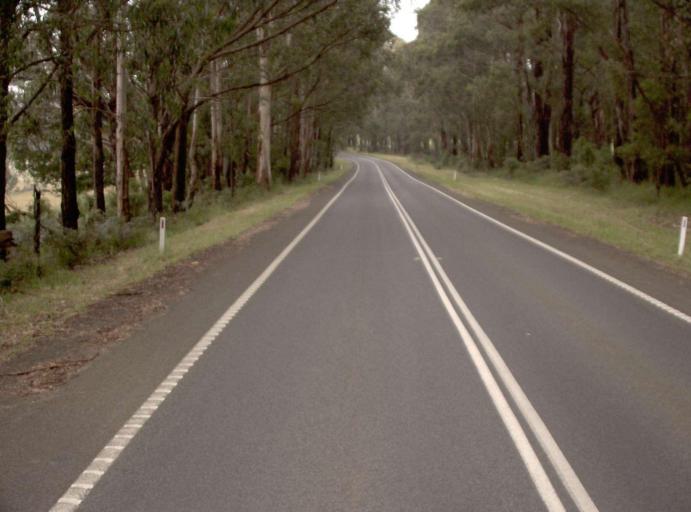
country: AU
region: Victoria
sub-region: Latrobe
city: Moe
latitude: -38.3311
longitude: 146.2373
